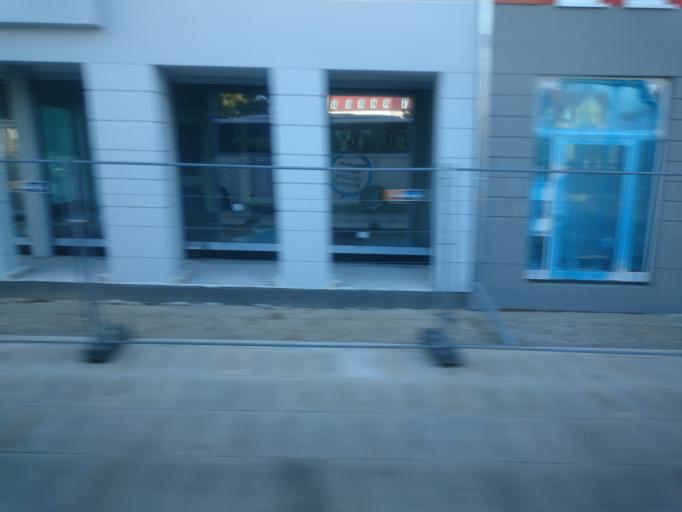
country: DE
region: Mecklenburg-Vorpommern
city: Anklam
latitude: 53.8560
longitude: 13.6888
